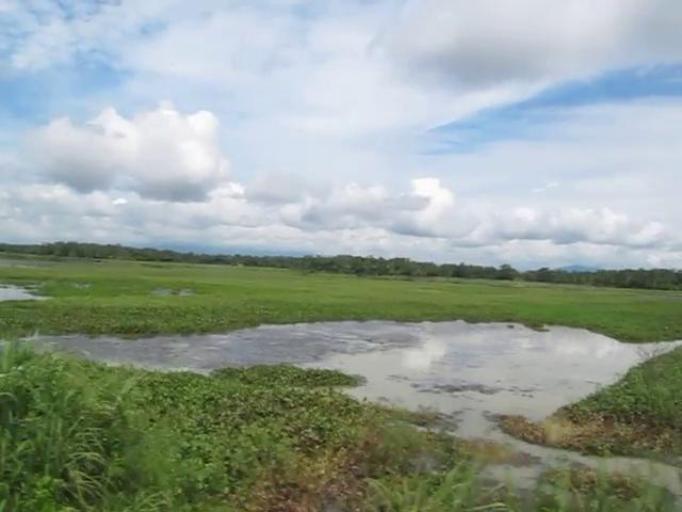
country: ID
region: Central Java
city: Meluwung
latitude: -7.3818
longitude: 108.6916
